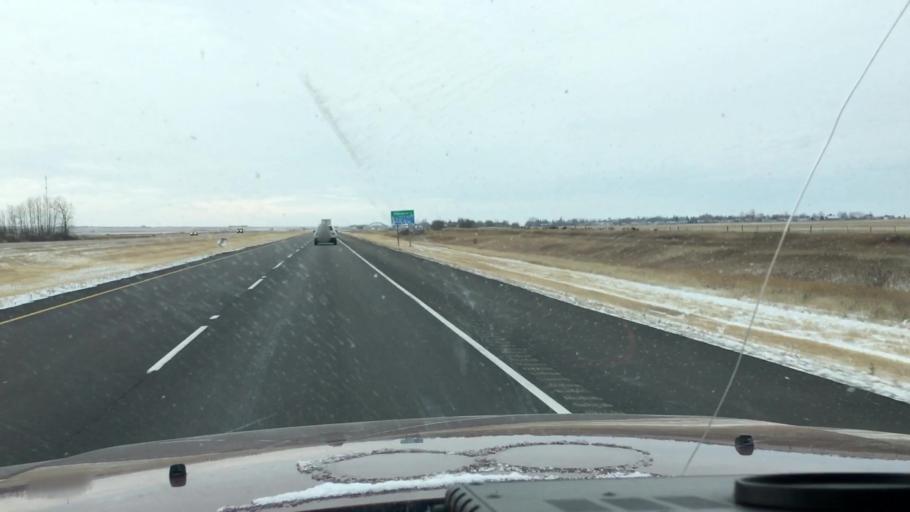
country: CA
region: Saskatchewan
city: Saskatoon
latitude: 51.8271
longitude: -106.5011
